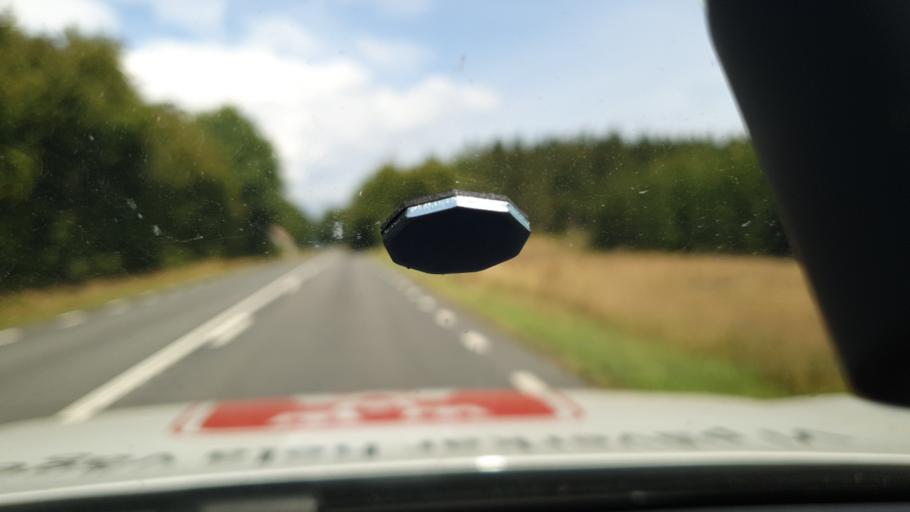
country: SE
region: Skane
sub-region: Simrishamns Kommun
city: Kivik
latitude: 55.6172
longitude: 14.1373
